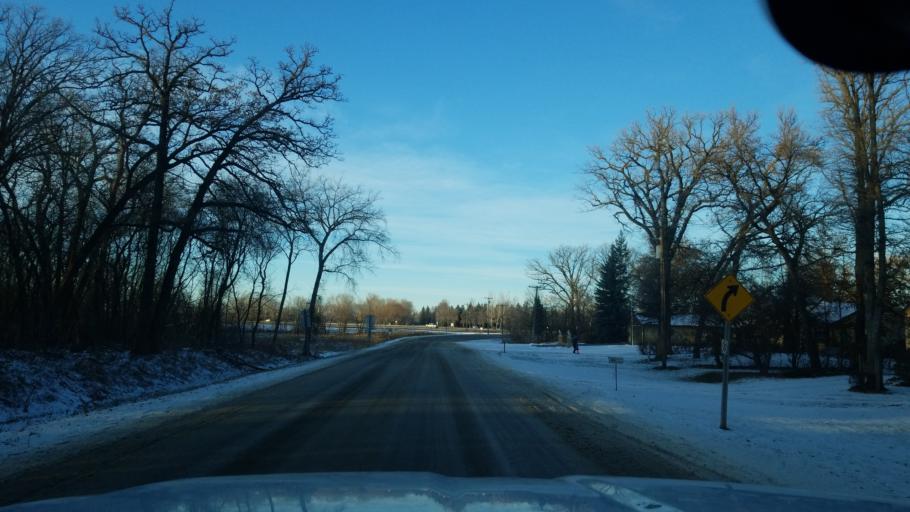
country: CA
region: Manitoba
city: Portage la Prairie
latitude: 49.9527
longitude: -98.3281
